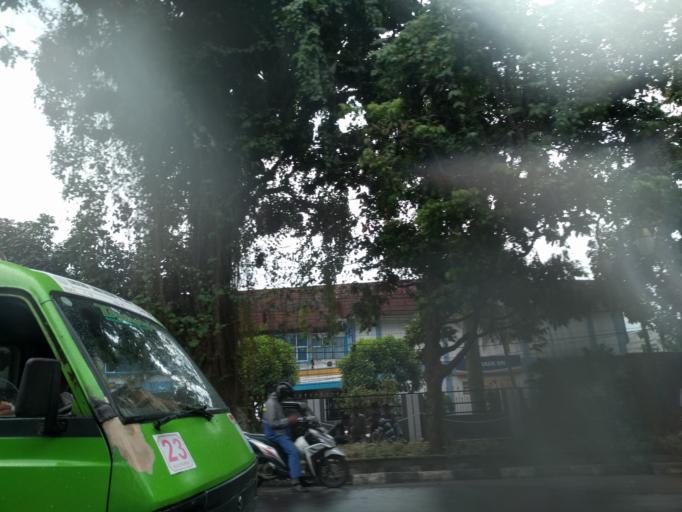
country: ID
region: West Java
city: Bogor
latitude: -6.6029
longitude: 106.7958
